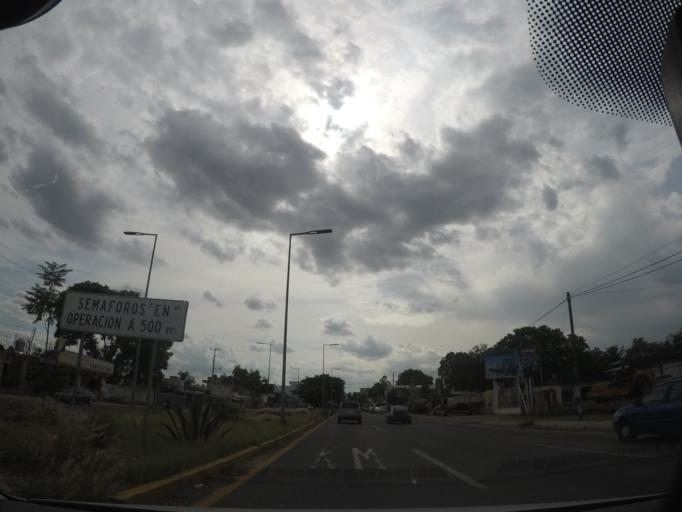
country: MX
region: Oaxaca
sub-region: Santa Cruz Amilpas
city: Santa Cruz Amilpas
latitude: 17.0640
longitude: -96.6747
